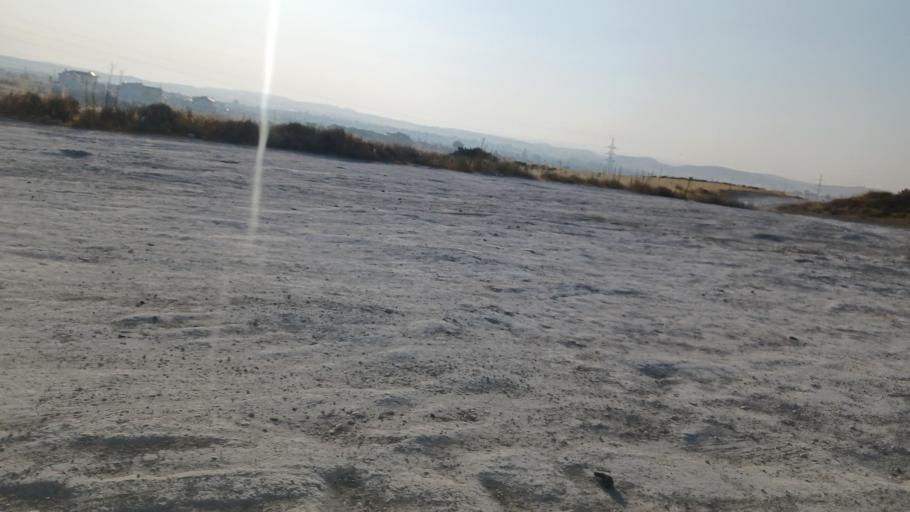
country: CY
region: Larnaka
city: Psevdas
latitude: 34.9264
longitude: 33.5149
